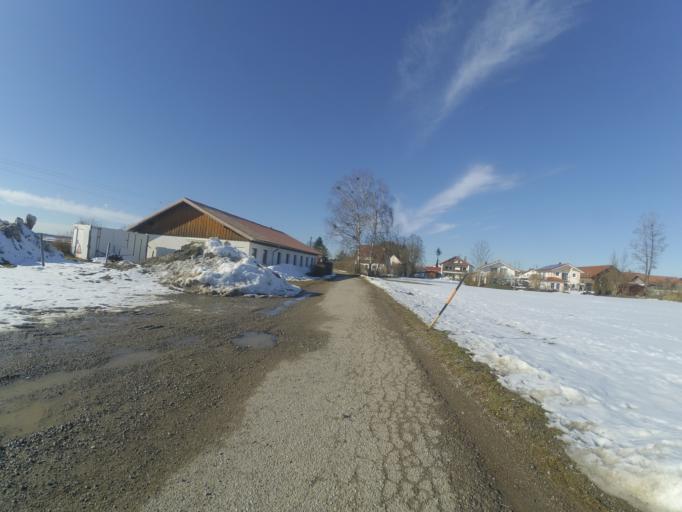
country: DE
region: Bavaria
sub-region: Upper Bavaria
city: Hohenkirchen-Siegertsbrunn
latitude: 47.9916
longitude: 11.7387
